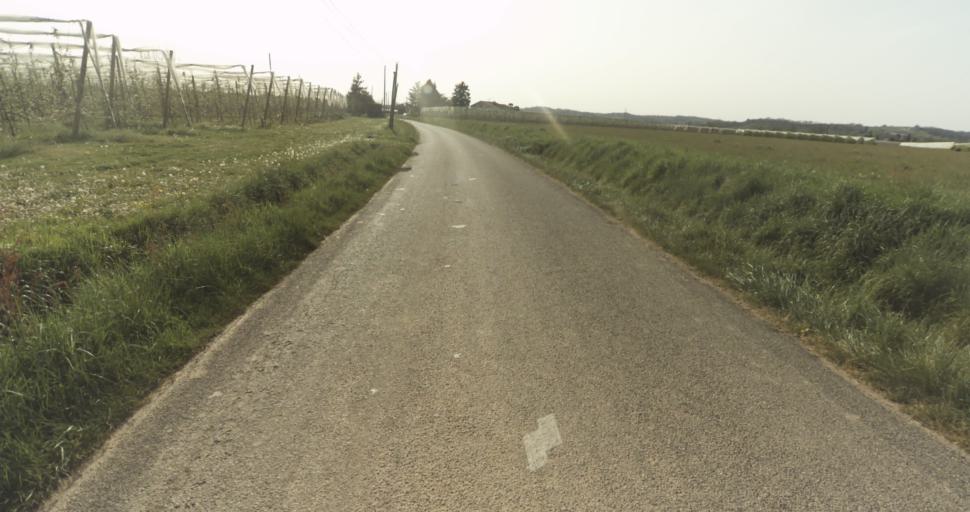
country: FR
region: Midi-Pyrenees
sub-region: Departement du Tarn-et-Garonne
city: Moissac
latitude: 44.1093
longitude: 1.1392
